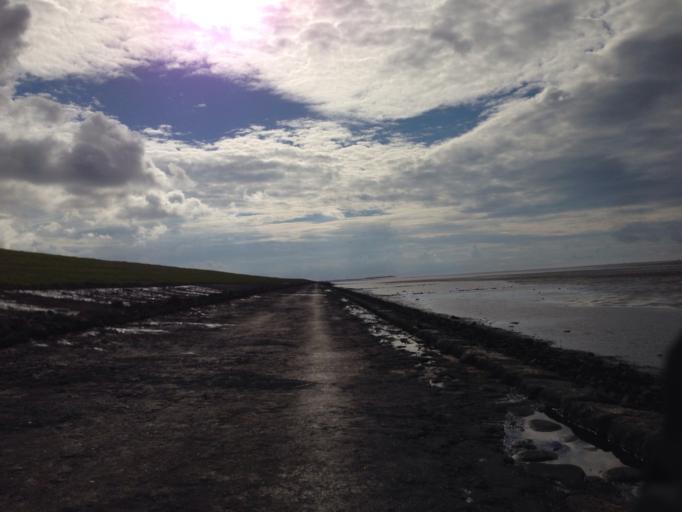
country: DE
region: Schleswig-Holstein
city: Dunsum
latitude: 54.7419
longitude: 8.4195
